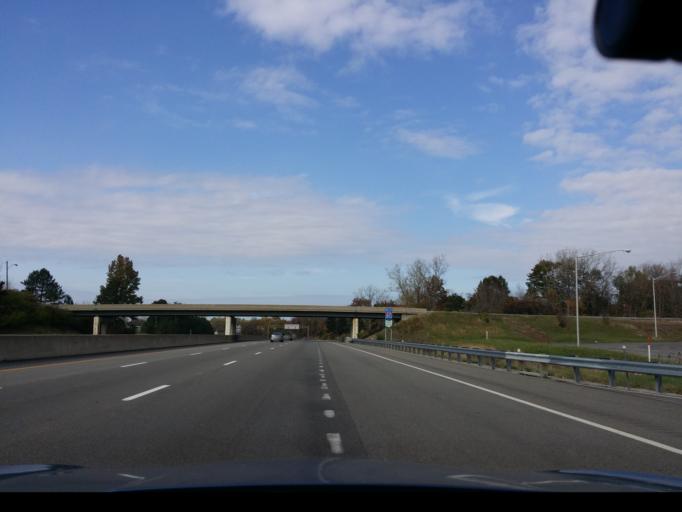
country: US
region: Ohio
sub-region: Cuyahoga County
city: Strongsville
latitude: 41.3372
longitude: -81.8230
